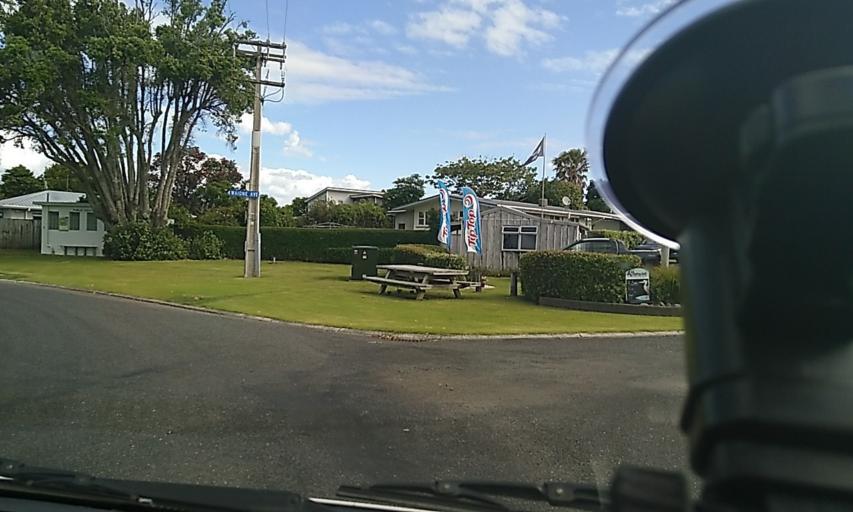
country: NZ
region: Bay of Plenty
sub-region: Western Bay of Plenty District
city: Waihi Beach
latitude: -37.4482
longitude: 175.9668
